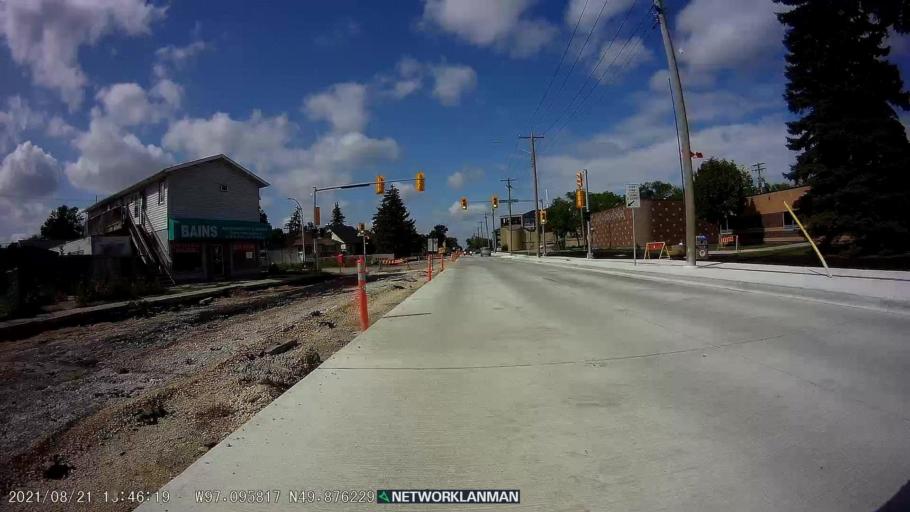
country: CA
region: Manitoba
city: Winnipeg
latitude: 49.8762
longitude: -97.0959
